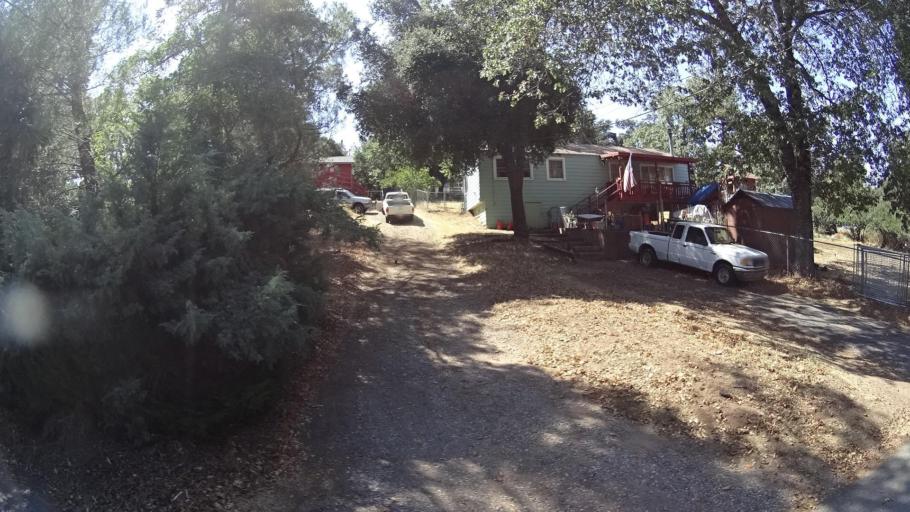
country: US
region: California
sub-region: San Diego County
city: Julian
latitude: 33.0861
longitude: -116.5875
